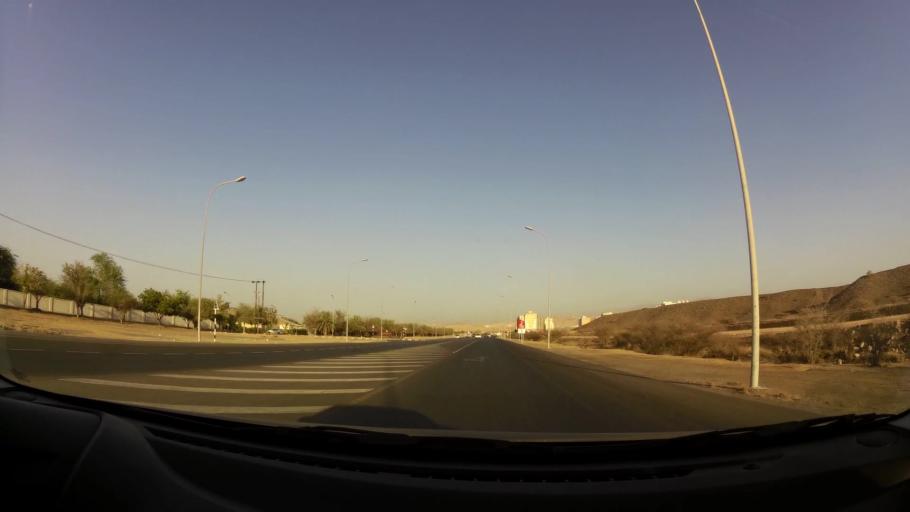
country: OM
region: Muhafazat Masqat
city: As Sib al Jadidah
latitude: 23.5809
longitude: 58.1744
